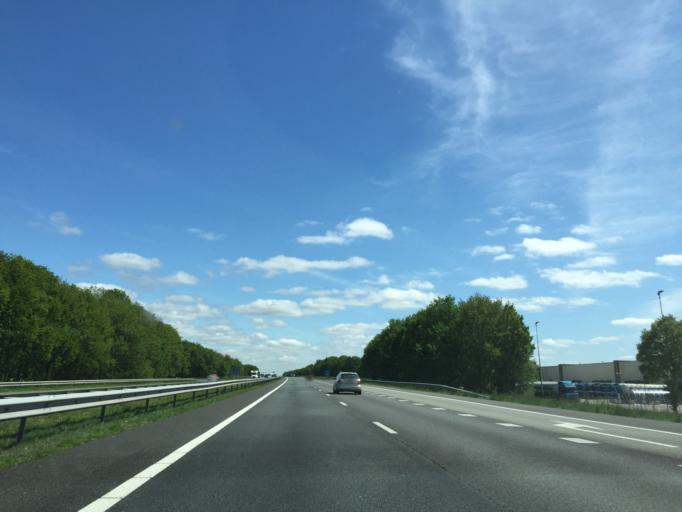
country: NL
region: Gelderland
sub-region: Gemeente Barneveld
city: Voorthuizen
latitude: 52.1685
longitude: 5.5889
